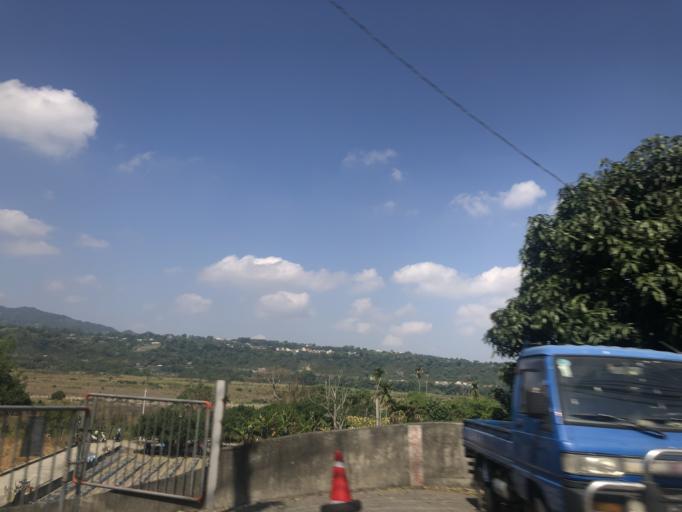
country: TW
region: Taiwan
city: Fengyuan
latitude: 24.2064
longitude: 120.8394
